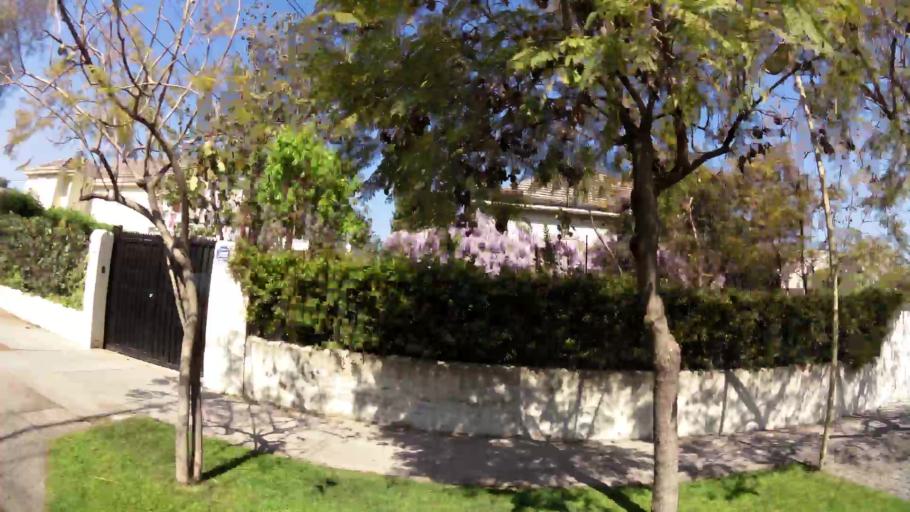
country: CL
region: Santiago Metropolitan
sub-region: Provincia de Santiago
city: Villa Presidente Frei, Nunoa, Santiago, Chile
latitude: -33.4222
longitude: -70.5903
